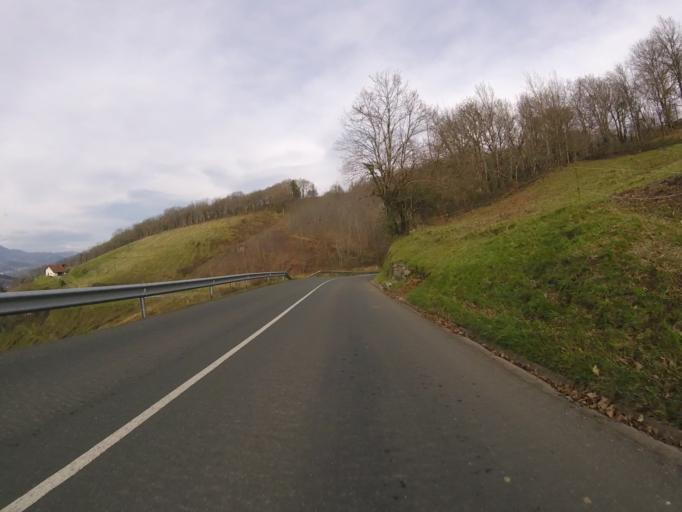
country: ES
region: Basque Country
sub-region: Provincia de Guipuzcoa
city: Azpeitia
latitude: 43.1702
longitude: -2.2381
